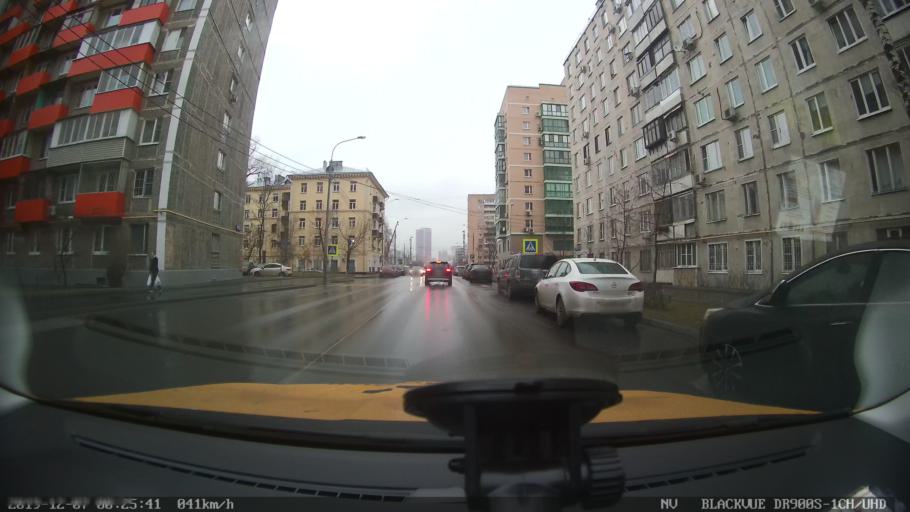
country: RU
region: Moscow
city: Rostokino
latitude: 55.8312
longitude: 37.6619
